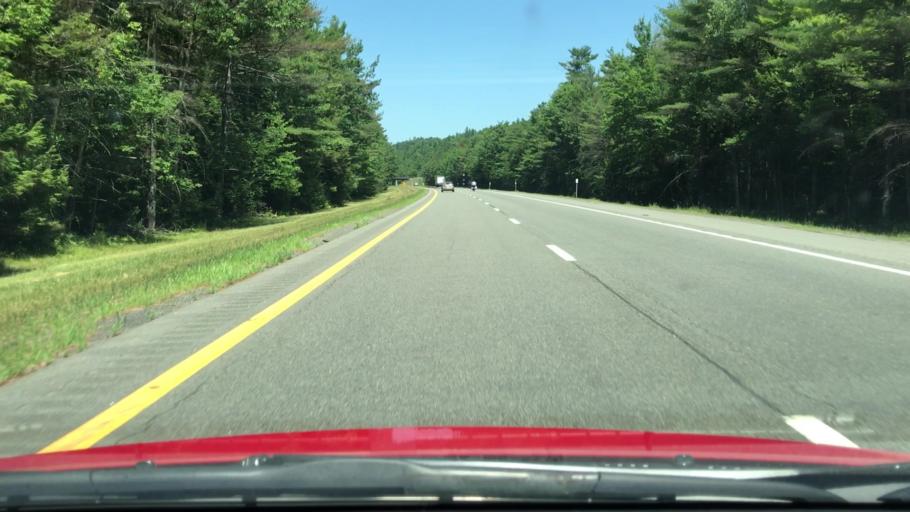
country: US
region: New York
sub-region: Essex County
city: Elizabethtown
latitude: 44.3201
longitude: -73.5281
